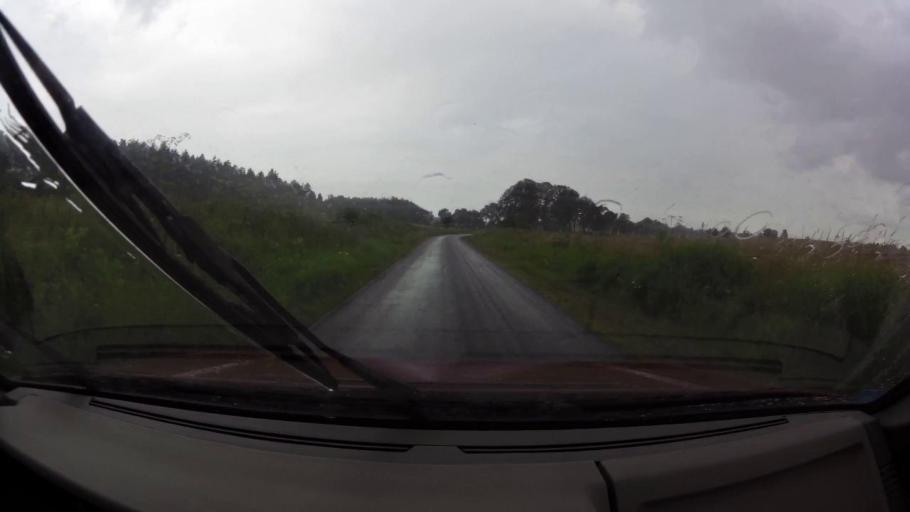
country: PL
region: West Pomeranian Voivodeship
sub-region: Koszalin
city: Koszalin
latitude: 54.0778
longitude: 16.1237
